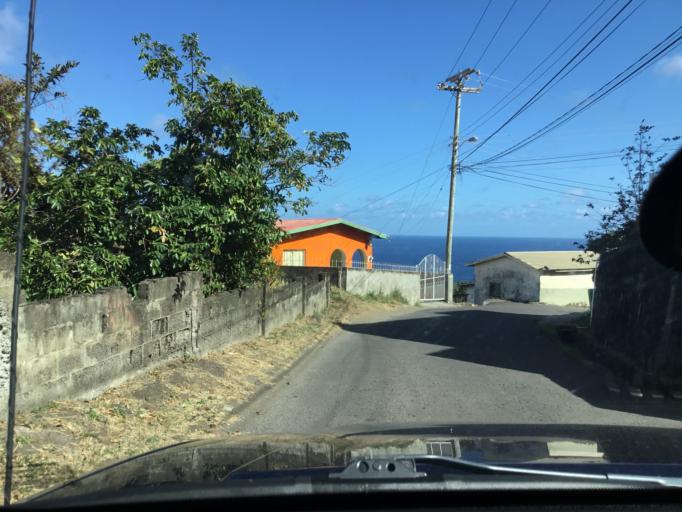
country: VC
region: Charlotte
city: Biabou
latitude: 13.1555
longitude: -61.1573
